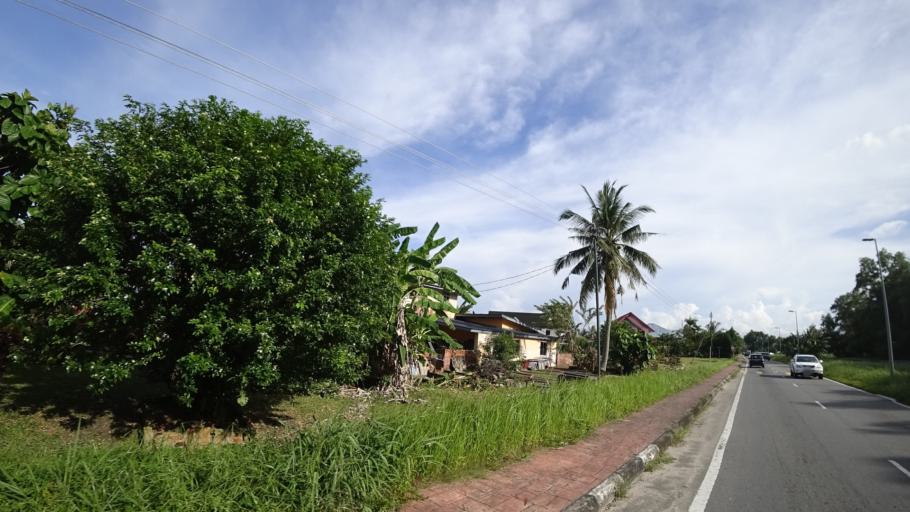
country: BN
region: Brunei and Muara
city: Bandar Seri Begawan
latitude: 4.9145
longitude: 114.9132
